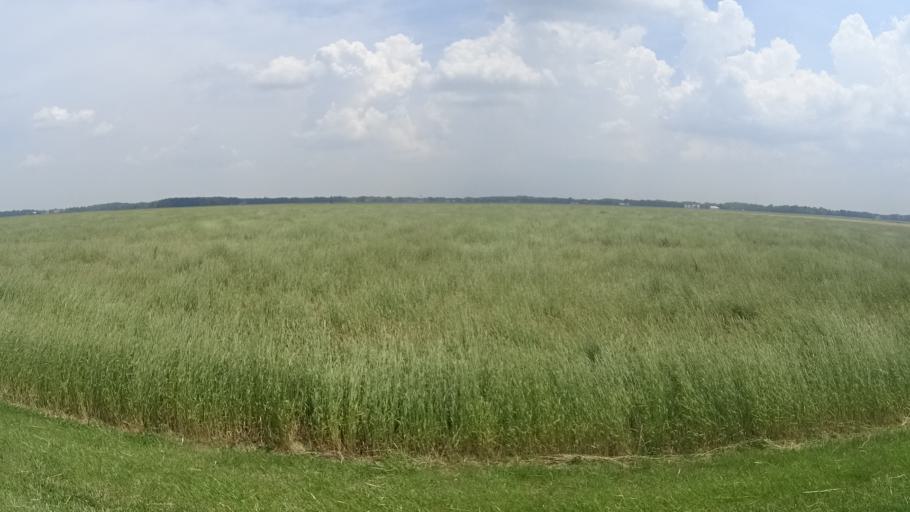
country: US
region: Ohio
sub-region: Huron County
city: Monroeville
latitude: 41.2939
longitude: -82.6923
